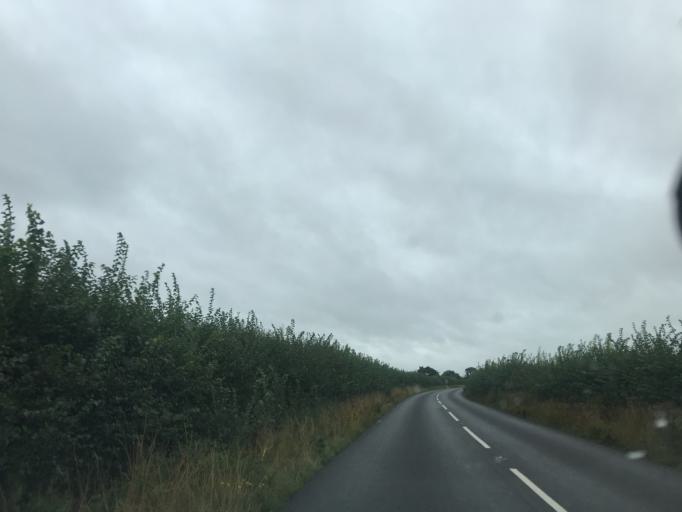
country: GB
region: England
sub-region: Buckinghamshire
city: Stone
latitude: 51.7884
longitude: -0.8694
